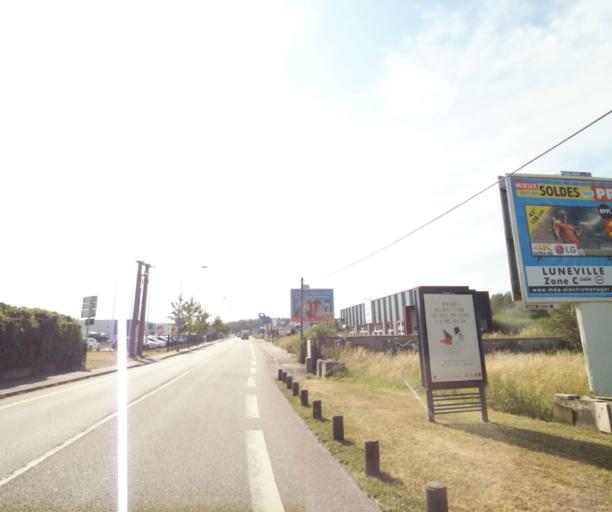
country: FR
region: Lorraine
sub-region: Departement de Meurthe-et-Moselle
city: Luneville
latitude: 48.5804
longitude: 6.5136
